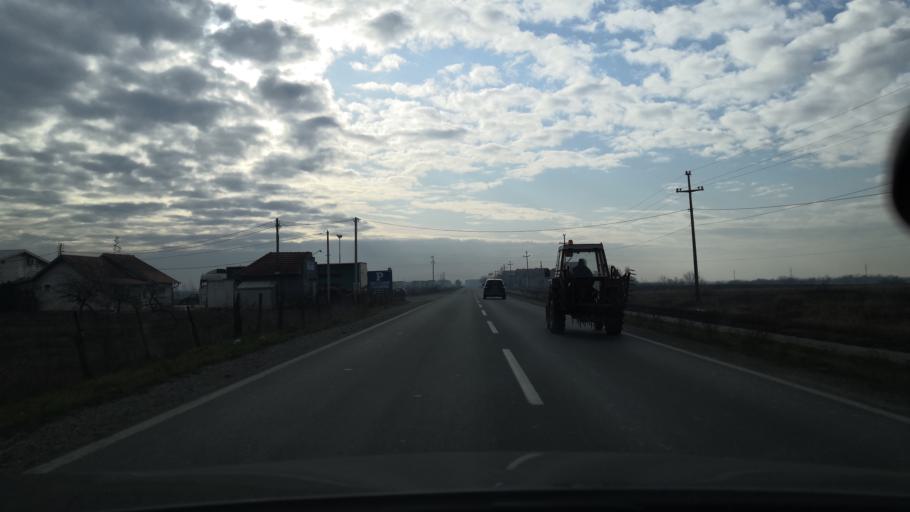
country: RS
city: Ugrinovci
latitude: 44.8640
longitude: 20.2047
